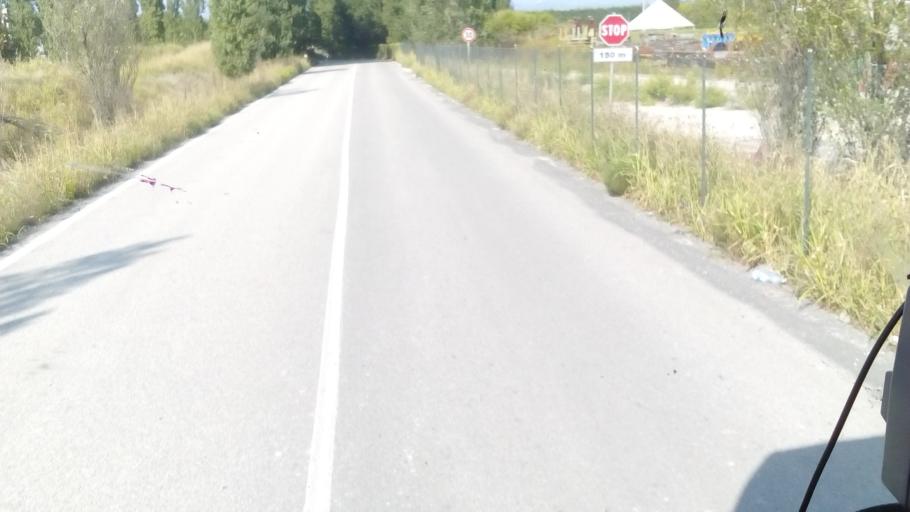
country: IT
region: Veneto
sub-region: Provincia di Verona
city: Campagnola
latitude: 45.3494
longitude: 11.0723
